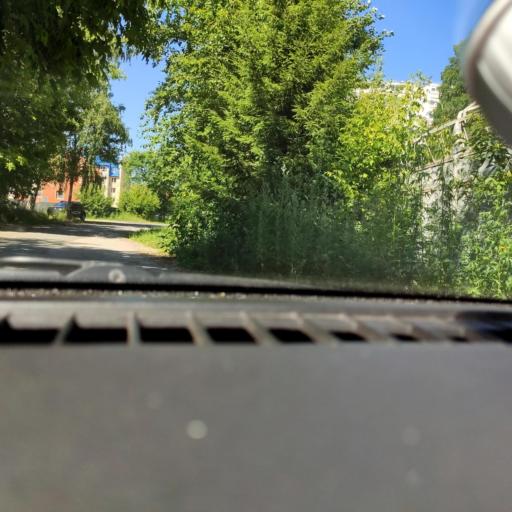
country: RU
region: Perm
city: Perm
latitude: 58.1181
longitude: 56.3810
